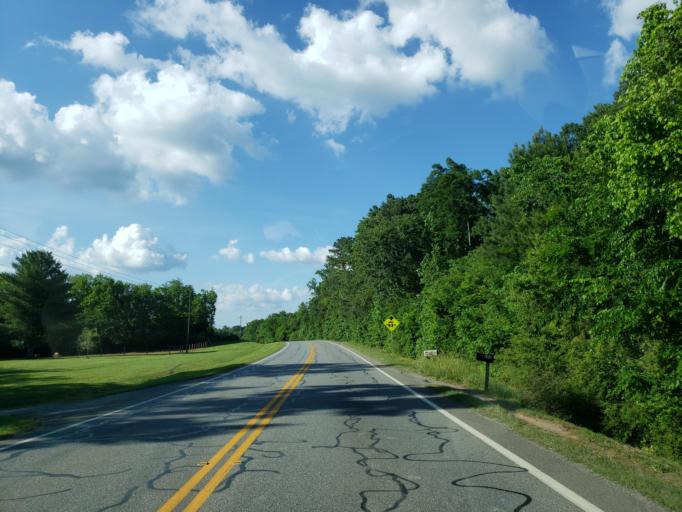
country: US
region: Georgia
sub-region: Bartow County
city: Rydal
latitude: 34.5221
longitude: -84.7073
